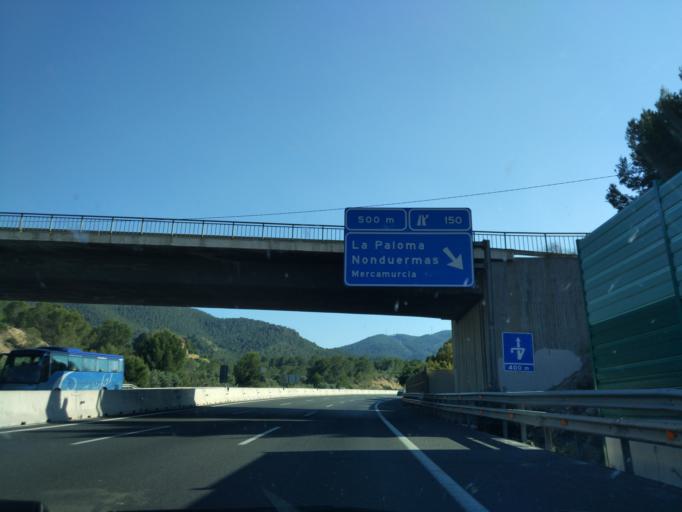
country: ES
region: Murcia
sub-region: Murcia
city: Murcia
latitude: 37.9250
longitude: -1.1572
